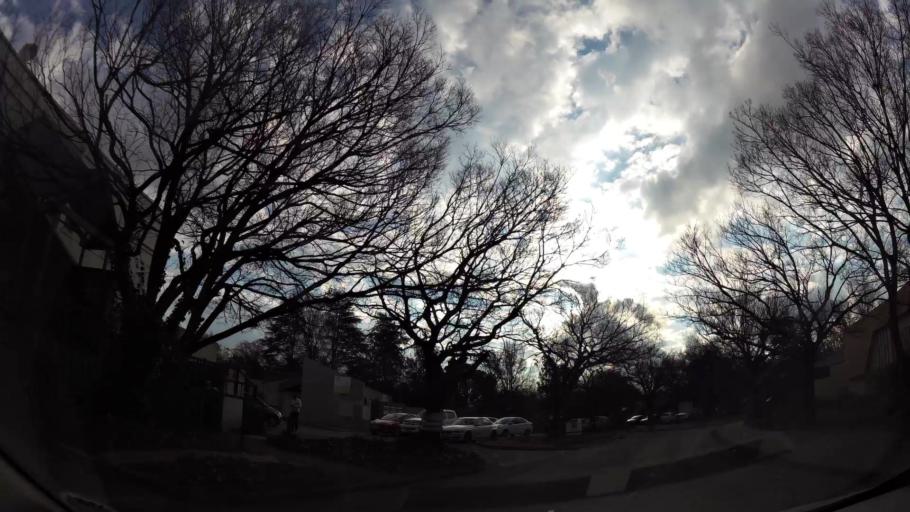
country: ZA
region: Orange Free State
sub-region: Fezile Dabi District Municipality
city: Sasolburg
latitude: -26.8118
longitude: 27.8260
